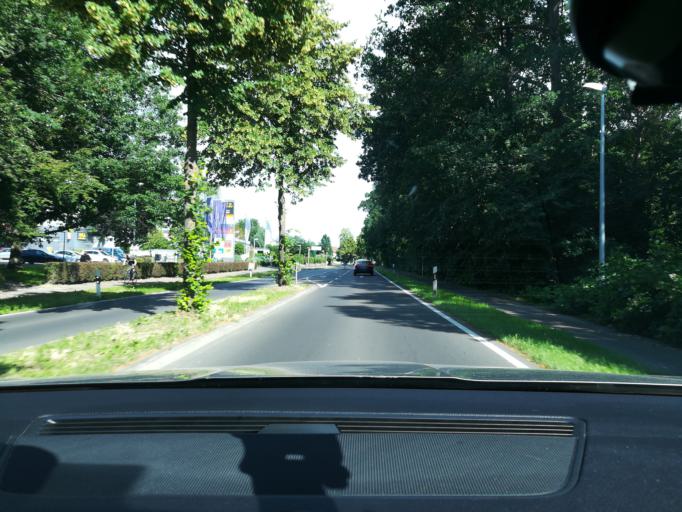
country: DE
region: North Rhine-Westphalia
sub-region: Regierungsbezirk Detmold
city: Minden
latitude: 52.3122
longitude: 8.8855
